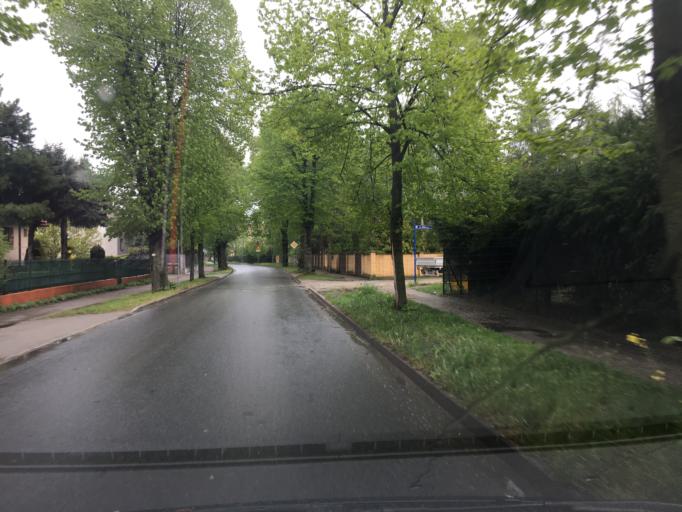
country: PL
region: Lower Silesian Voivodeship
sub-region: Powiat wroclawski
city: Zerniki Wroclawskie
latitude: 51.0321
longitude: 17.0577
